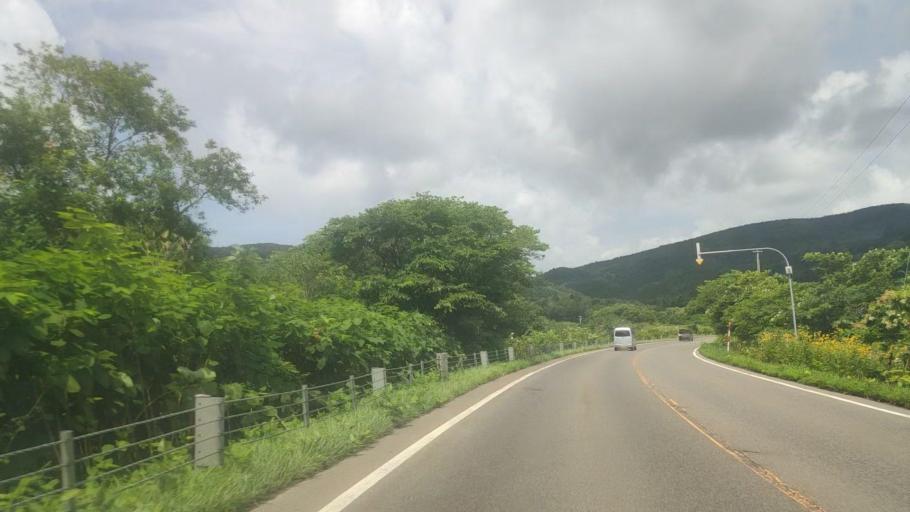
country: JP
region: Hokkaido
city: Niseko Town
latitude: 42.5872
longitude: 140.4493
